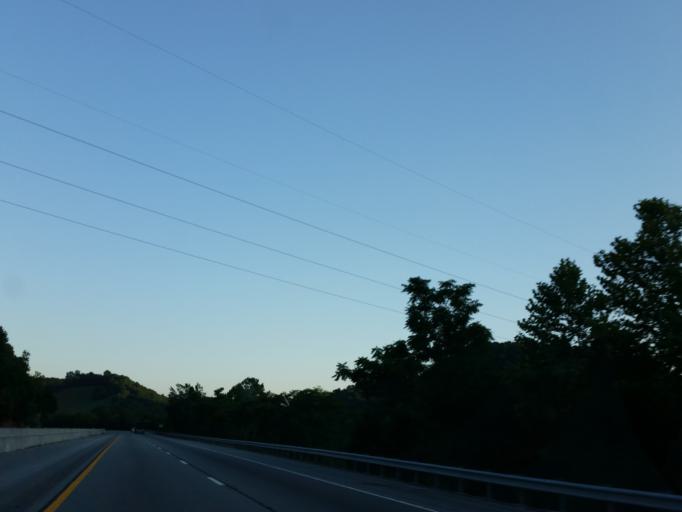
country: US
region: Tennessee
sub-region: Putnam County
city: Lafayette
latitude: 36.1232
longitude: -85.7775
